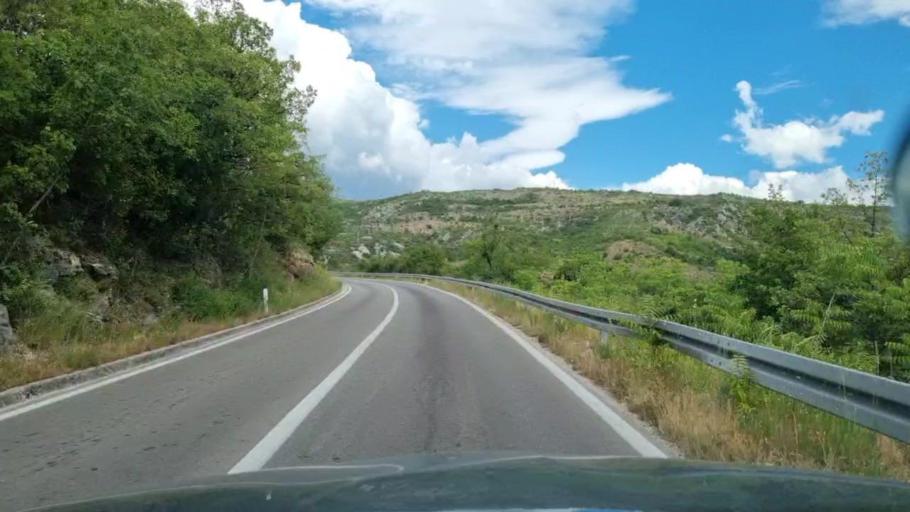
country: BA
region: Federation of Bosnia and Herzegovina
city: Blagaj
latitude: 43.2613
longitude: 17.9235
